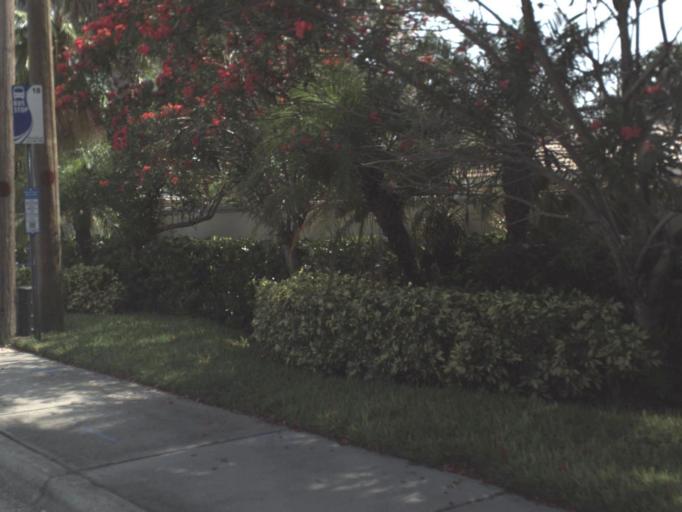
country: US
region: Florida
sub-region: Pinellas County
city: Seminole
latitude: 27.8444
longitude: -82.7870
